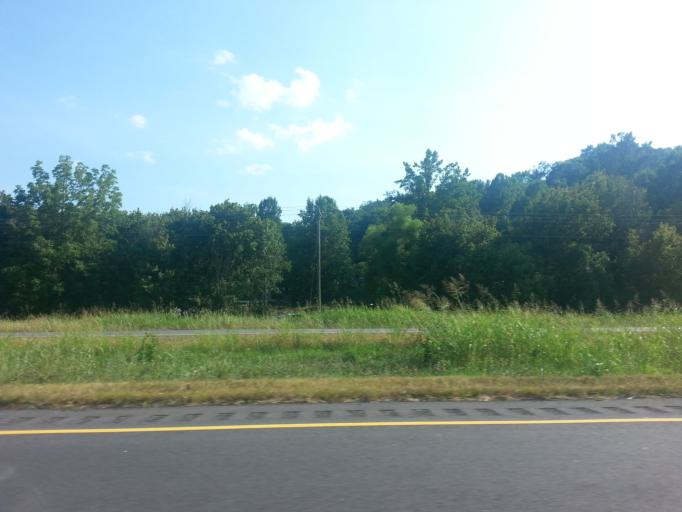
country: US
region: Tennessee
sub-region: Loudon County
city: Greenback
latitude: 35.7532
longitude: -84.1258
